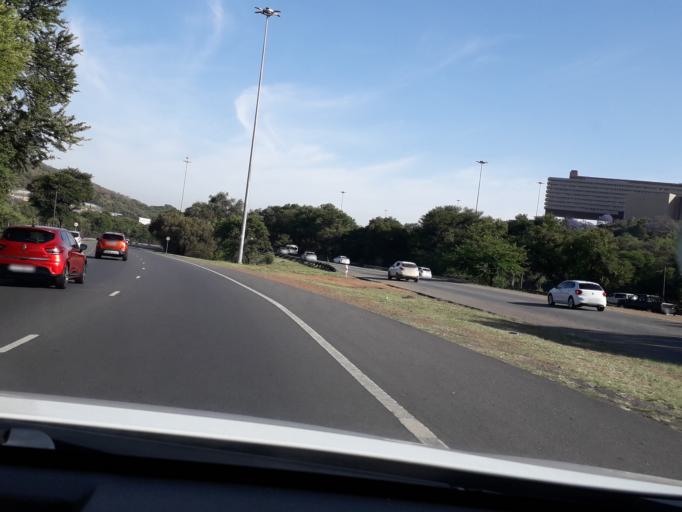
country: ZA
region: Gauteng
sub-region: City of Tshwane Metropolitan Municipality
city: Pretoria
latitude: -25.7709
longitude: 28.1974
